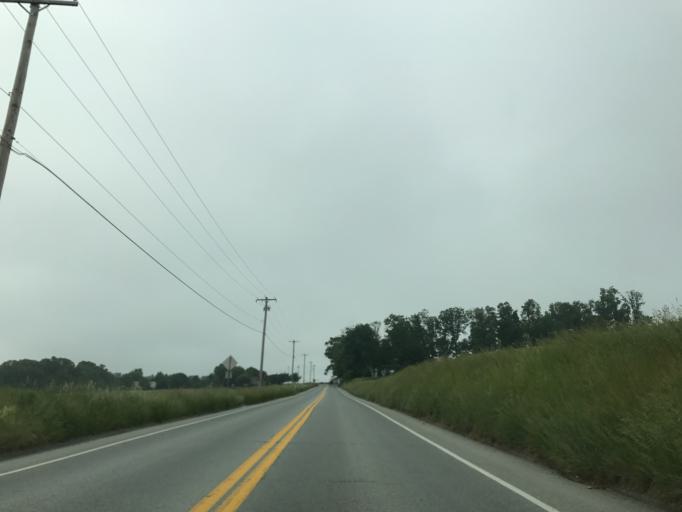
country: US
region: Pennsylvania
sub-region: York County
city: Susquehanna Trails
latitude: 39.8426
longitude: -76.4204
